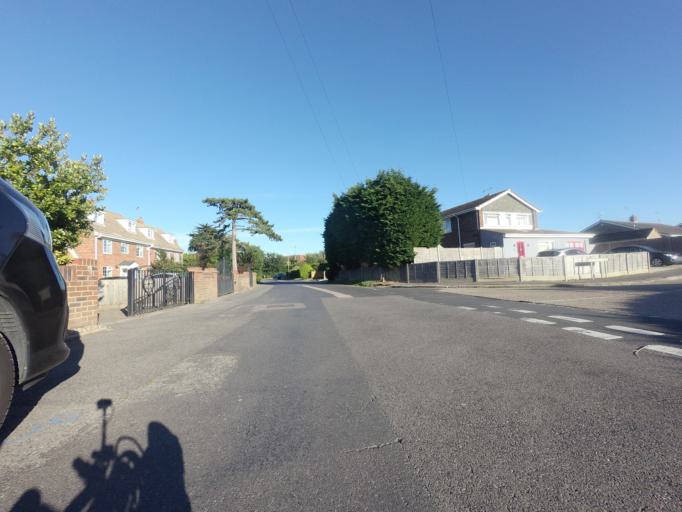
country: GB
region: England
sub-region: Kent
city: Herne Bay
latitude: 51.3584
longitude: 1.1390
